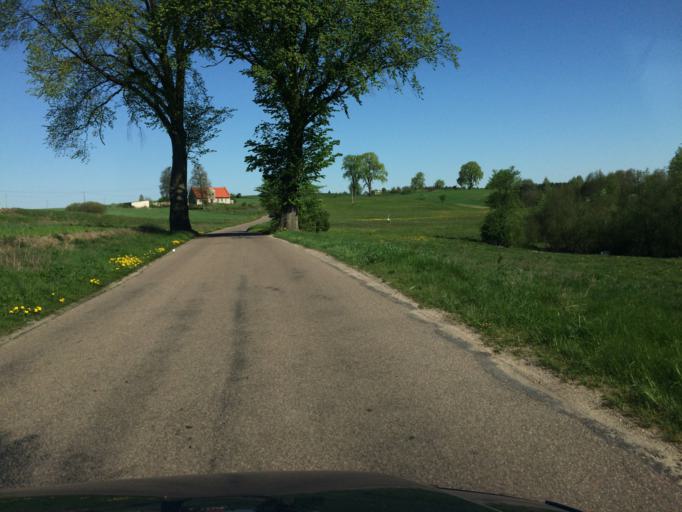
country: PL
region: Warmian-Masurian Voivodeship
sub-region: Powiat dzialdowski
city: Rybno
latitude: 53.4269
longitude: 19.9201
